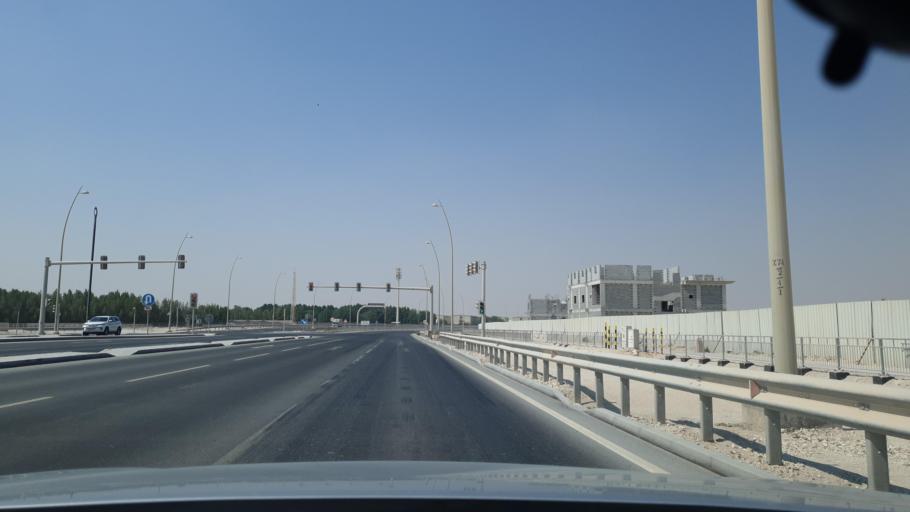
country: QA
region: Al Khawr
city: Al Khawr
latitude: 25.6608
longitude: 51.4854
